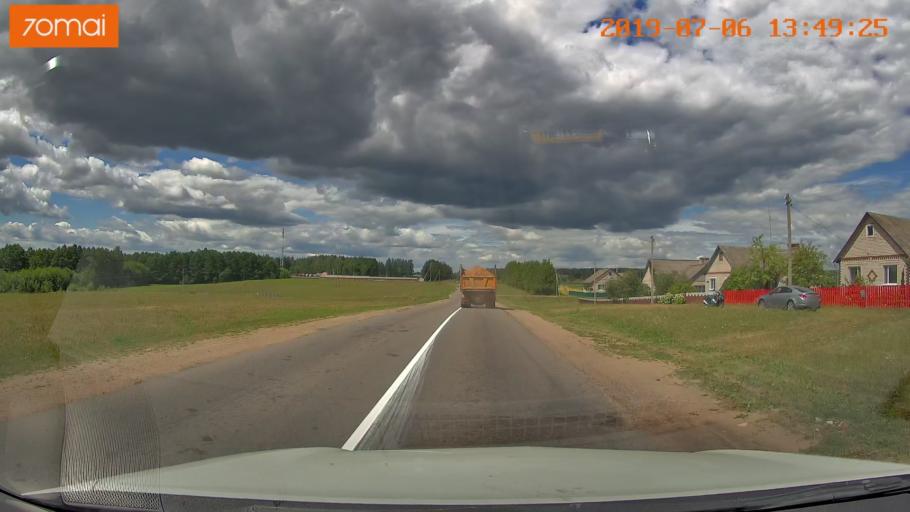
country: BY
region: Minsk
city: Ivyanyets
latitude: 53.6938
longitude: 26.8519
